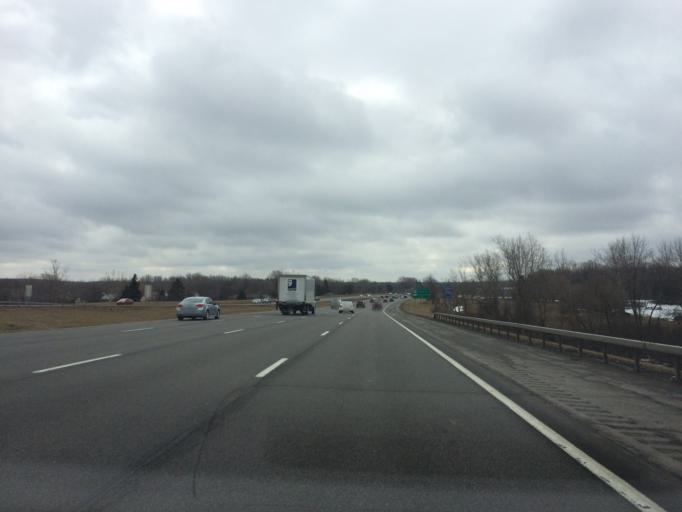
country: US
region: New York
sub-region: Monroe County
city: Rochester
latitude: 43.1045
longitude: -77.6010
